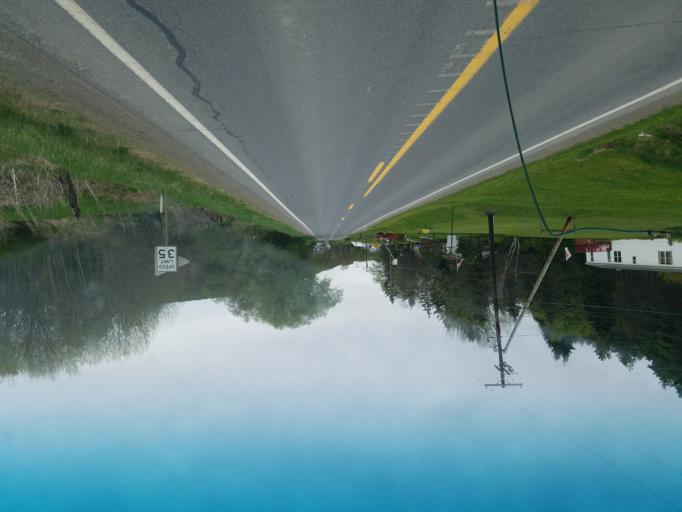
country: US
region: Pennsylvania
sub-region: Tioga County
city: Westfield
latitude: 41.8659
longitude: -77.5343
